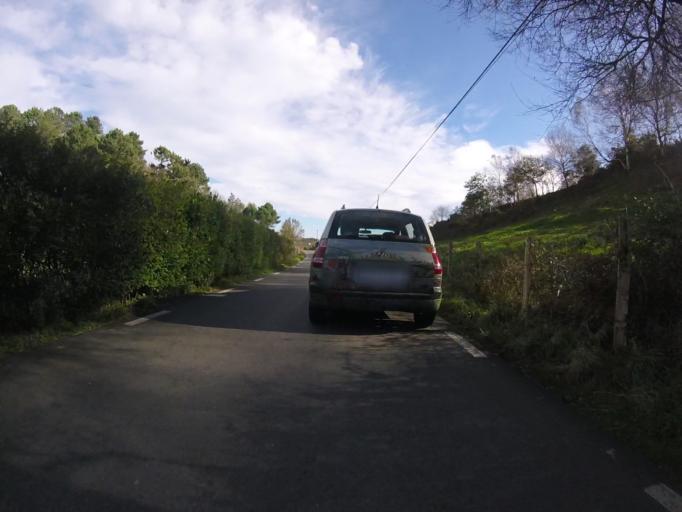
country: ES
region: Basque Country
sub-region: Provincia de Guipuzcoa
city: Usurbil
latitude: 43.3019
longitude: -2.0532
